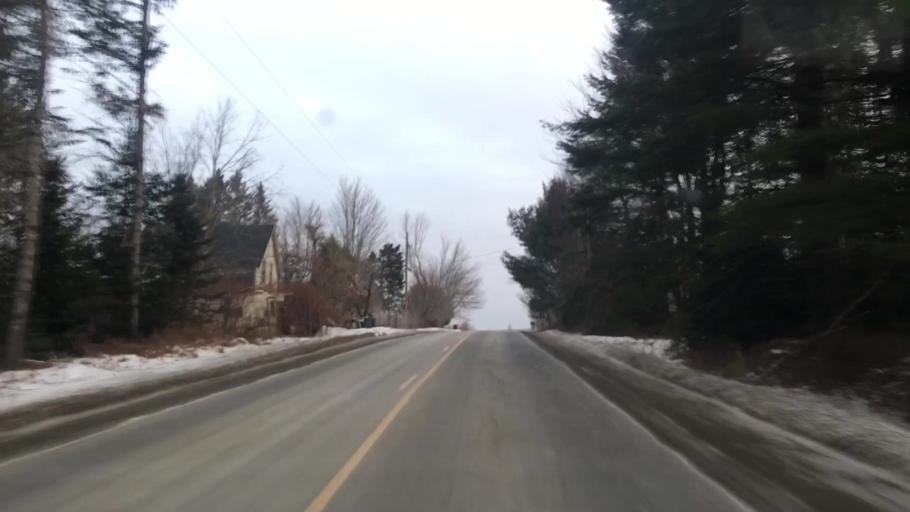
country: US
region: Maine
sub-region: Hancock County
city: Franklin
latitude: 44.6821
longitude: -68.3518
